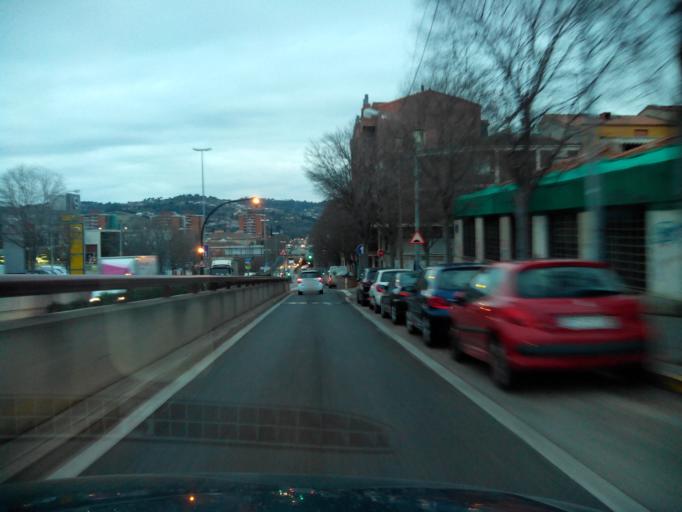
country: ES
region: Catalonia
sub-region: Provincia de Barcelona
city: Terrassa
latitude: 41.5518
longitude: 2.0247
